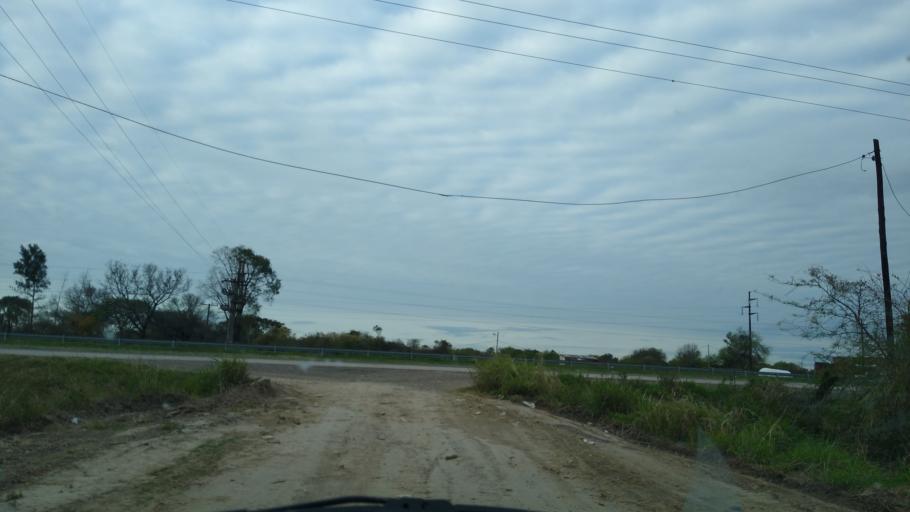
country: AR
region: Chaco
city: Fontana
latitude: -27.3809
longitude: -59.0393
